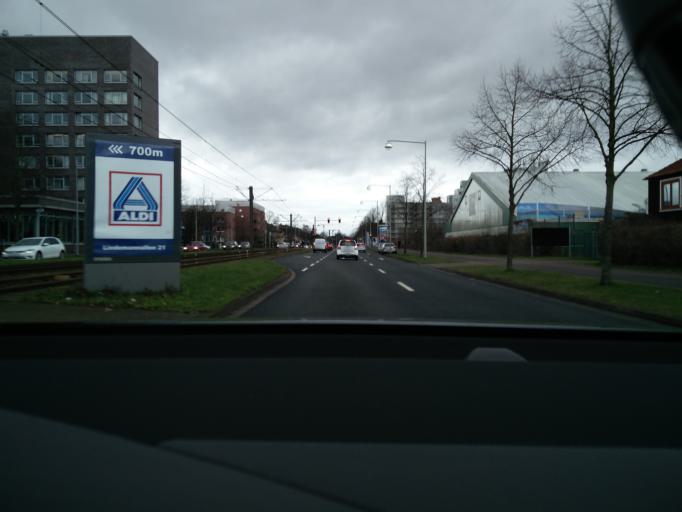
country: DE
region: Lower Saxony
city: Hannover
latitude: 52.3629
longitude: 9.7770
